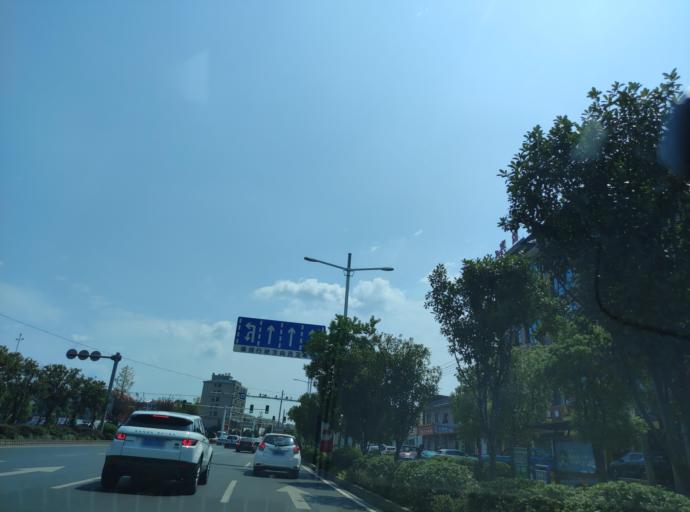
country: CN
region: Jiangxi Sheng
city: Pingxiang
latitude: 27.6584
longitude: 113.8956
